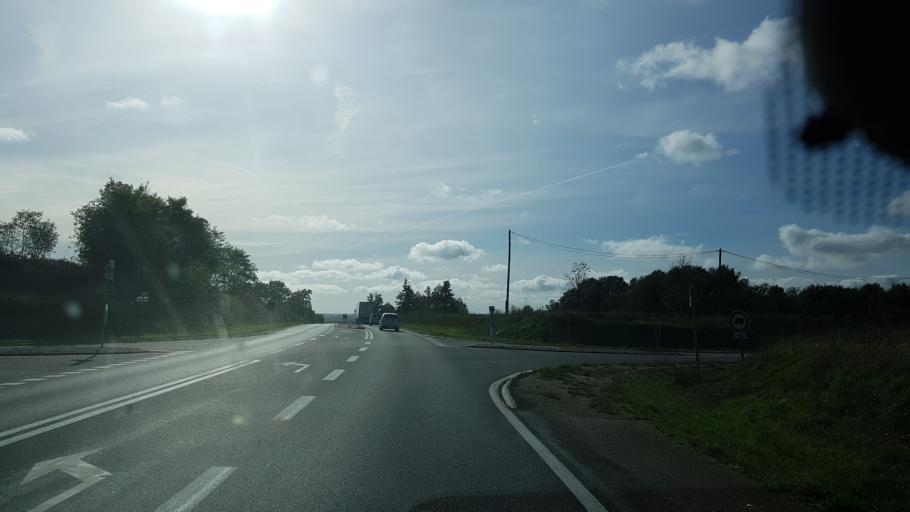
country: FR
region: Poitou-Charentes
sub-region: Departement de la Charente
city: Saint-Claud
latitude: 45.9073
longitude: 0.4879
